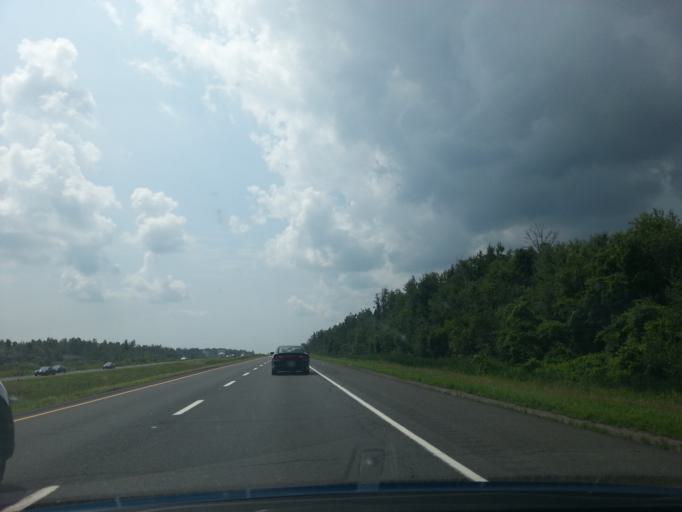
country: CA
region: Quebec
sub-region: Chaudiere-Appalaches
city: Saint-Antoine-de-Tilly
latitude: 46.6041
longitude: -71.5294
